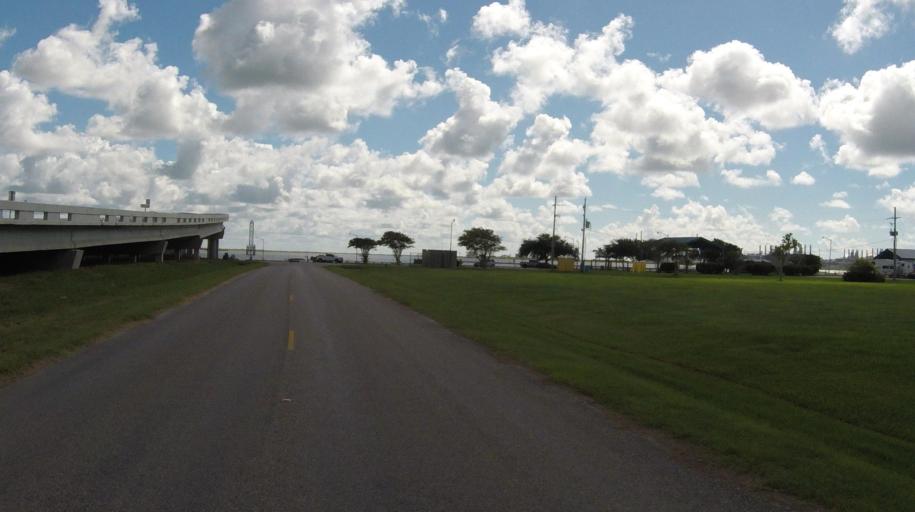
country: US
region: Texas
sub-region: Jefferson County
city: Port Arthur
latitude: 29.7636
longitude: -93.9003
